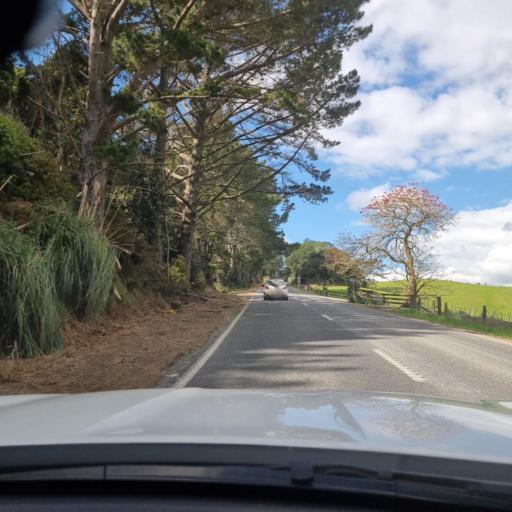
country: NZ
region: Northland
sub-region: Kaipara District
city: Dargaville
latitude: -36.1950
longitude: 174.0450
